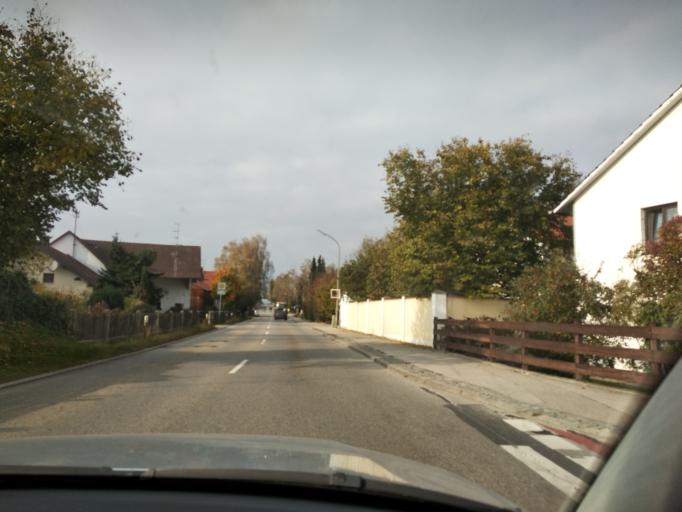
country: DE
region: Bavaria
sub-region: Upper Bavaria
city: Forstinning
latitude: 48.1654
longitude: 11.8948
